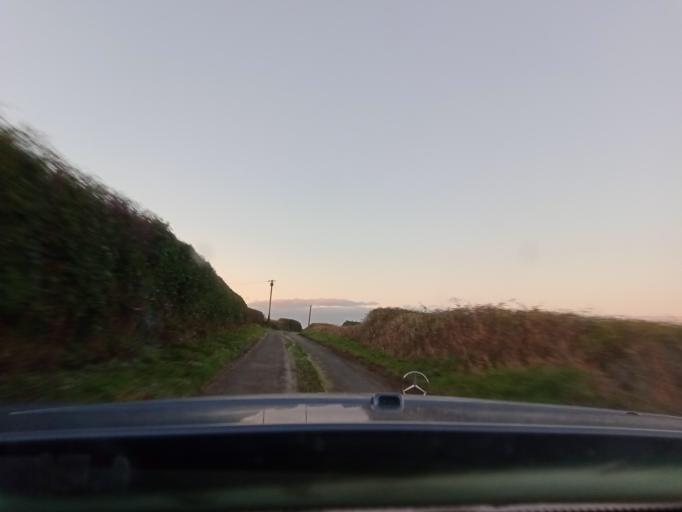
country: IE
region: Leinster
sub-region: Kilkenny
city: Graiguenamanagh
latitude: 52.5795
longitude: -6.9604
